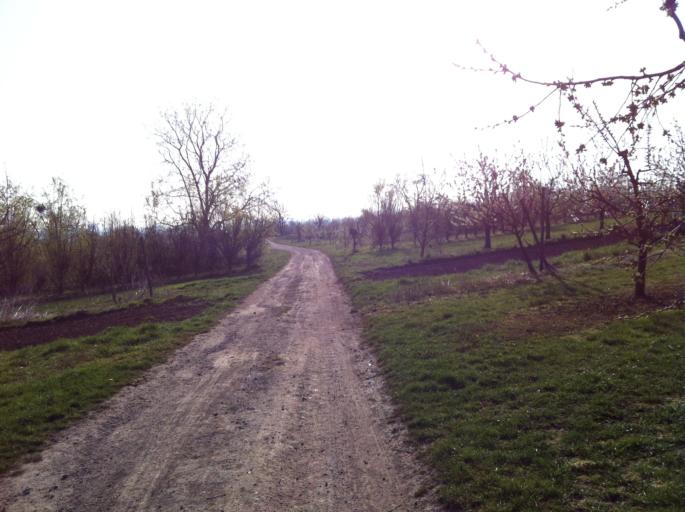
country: DE
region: Rheinland-Pfalz
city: Budenheim
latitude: 49.9842
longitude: 8.1961
